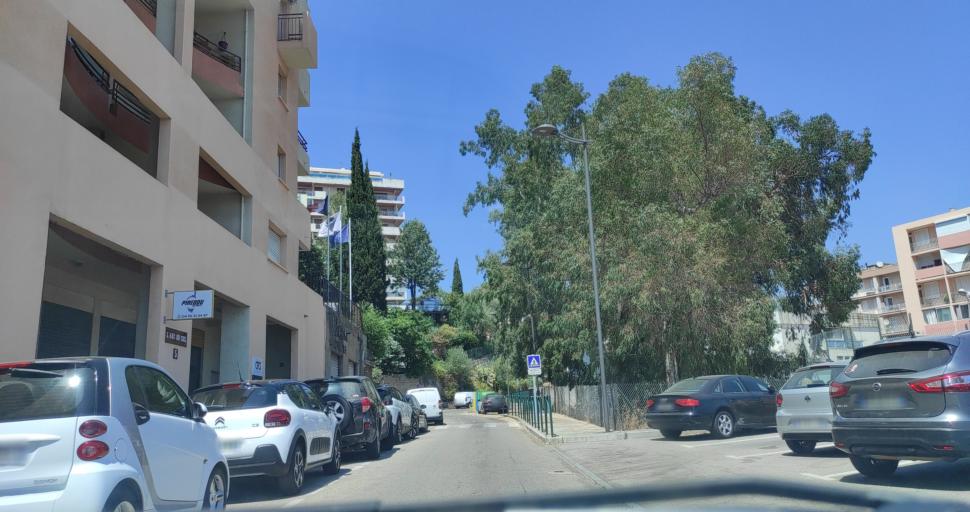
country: FR
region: Corsica
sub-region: Departement de la Corse-du-Sud
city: Ajaccio
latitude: 41.9328
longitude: 8.7406
